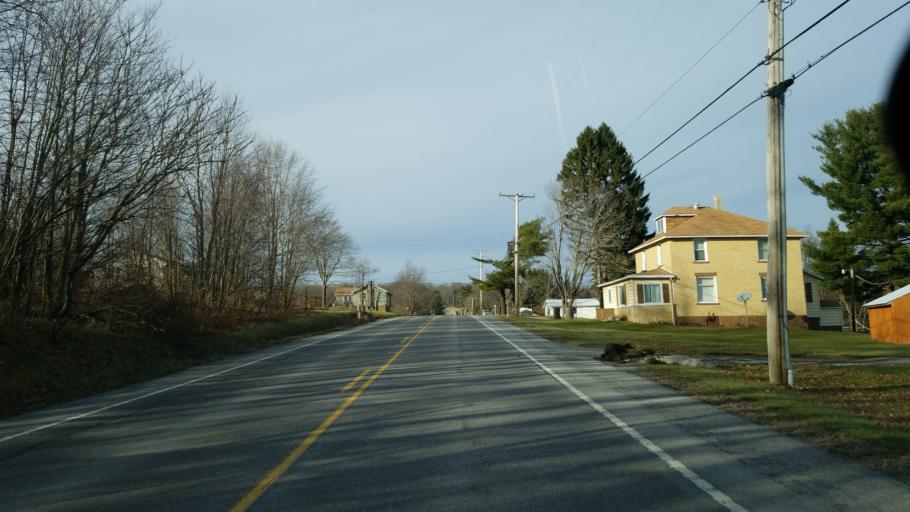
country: US
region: Pennsylvania
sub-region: Clearfield County
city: Curwensville
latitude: 41.0043
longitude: -78.6365
